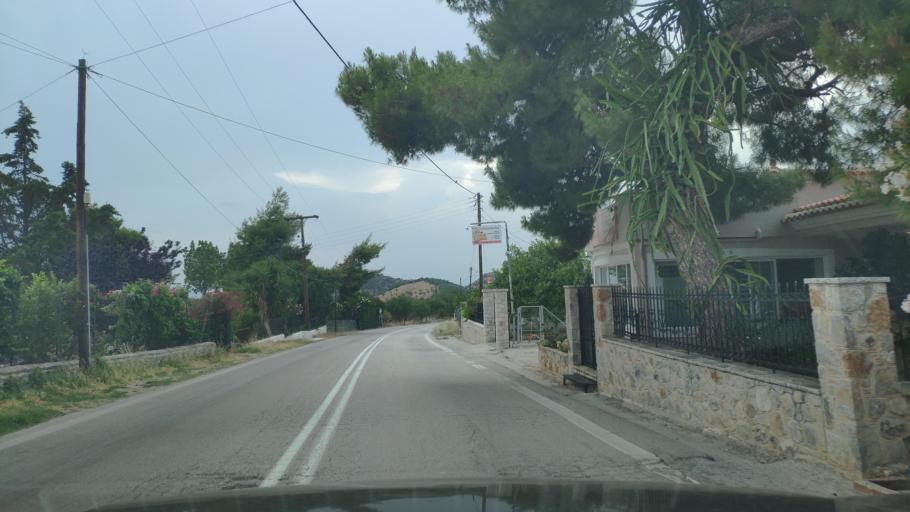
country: GR
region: Peloponnese
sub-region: Nomos Argolidos
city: Didyma
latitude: 37.4311
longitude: 23.1755
